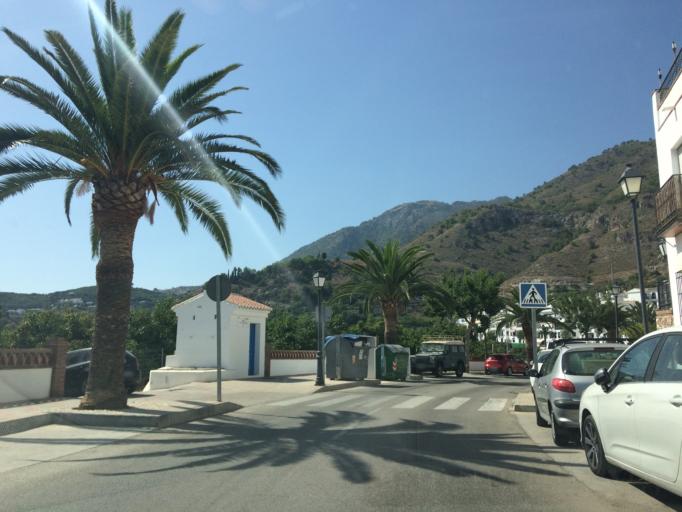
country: ES
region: Andalusia
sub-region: Provincia de Malaga
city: Frigiliana
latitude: 36.7929
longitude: -3.8997
